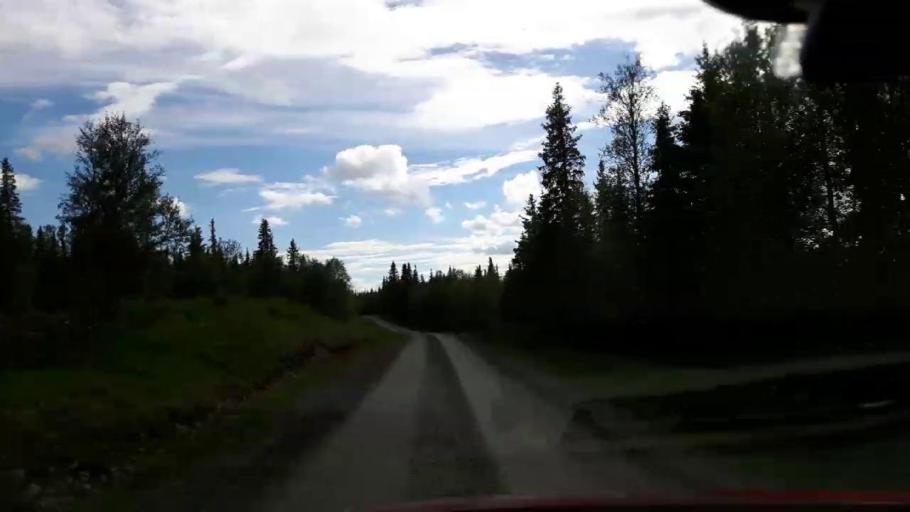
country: SE
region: Jaemtland
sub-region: Krokoms Kommun
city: Valla
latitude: 63.8685
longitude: 14.1181
